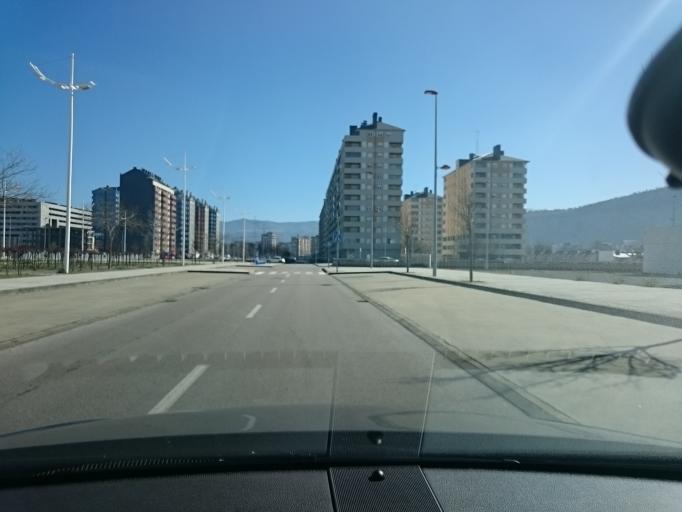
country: ES
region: Castille and Leon
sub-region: Provincia de Leon
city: Ponferrada
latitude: 42.5557
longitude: -6.6074
